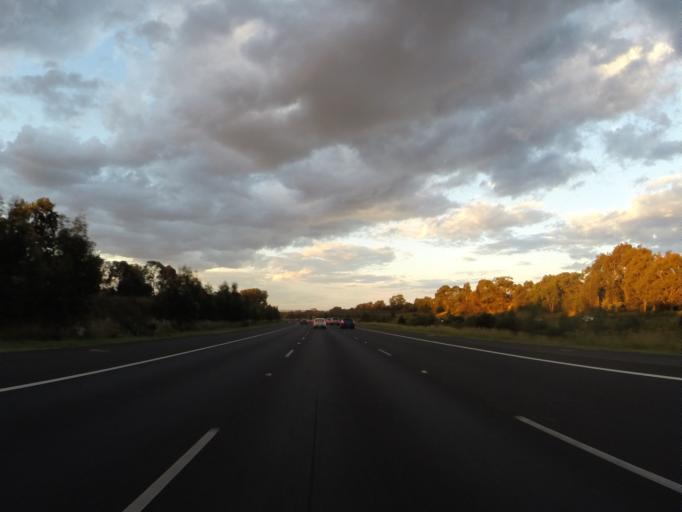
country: AU
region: New South Wales
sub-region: Campbelltown Municipality
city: Leumeah
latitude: -34.0483
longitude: 150.8162
